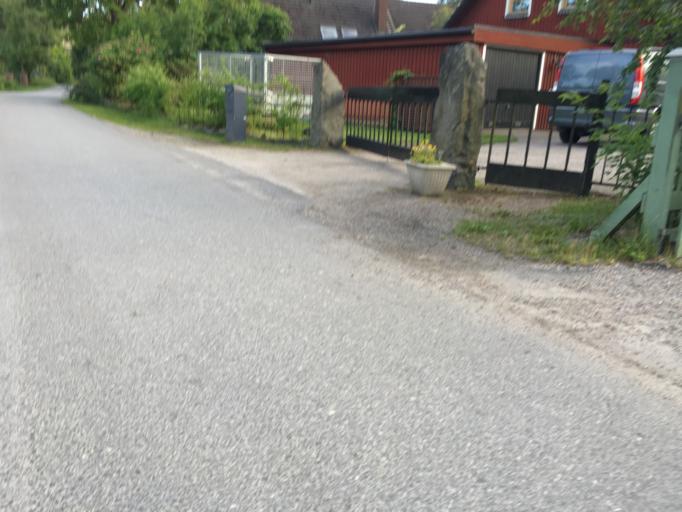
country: SE
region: Stockholm
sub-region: Nacka Kommun
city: Fisksatra
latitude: 59.3185
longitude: 18.2373
